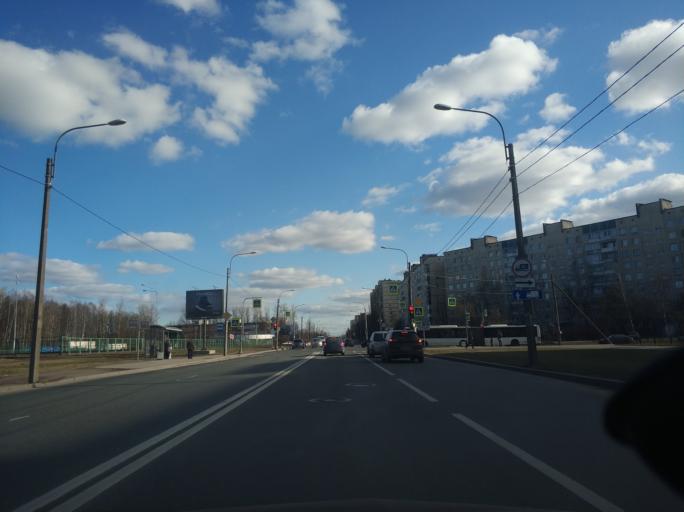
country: RU
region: St.-Petersburg
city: Krasnogvargeisky
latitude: 59.9576
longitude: 30.4931
